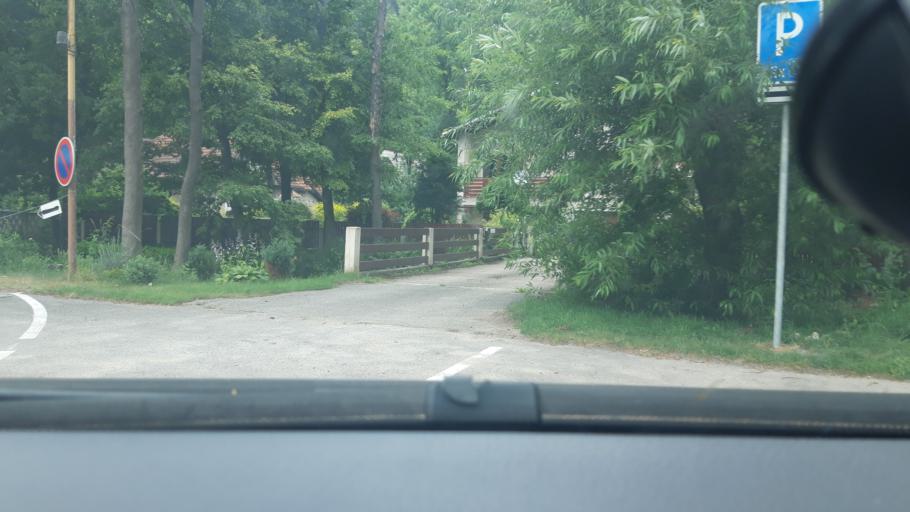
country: SK
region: Zilinsky
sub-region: Okres Martin
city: Martin
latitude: 48.9320
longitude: 18.9315
